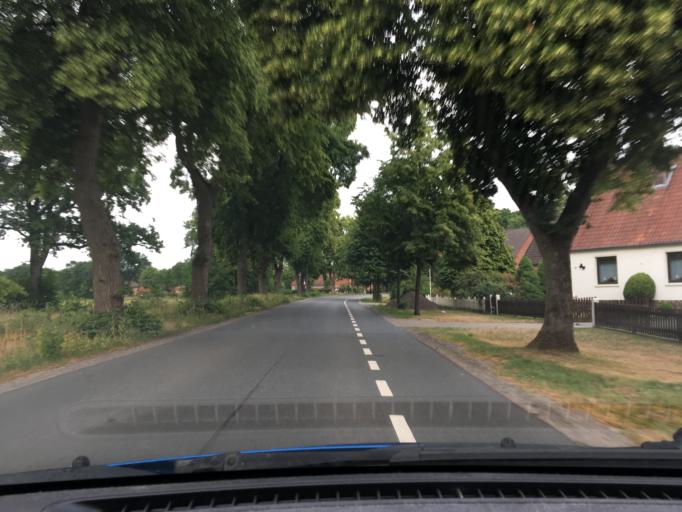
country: DE
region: Lower Saxony
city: Walsrode
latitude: 52.8272
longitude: 9.6182
